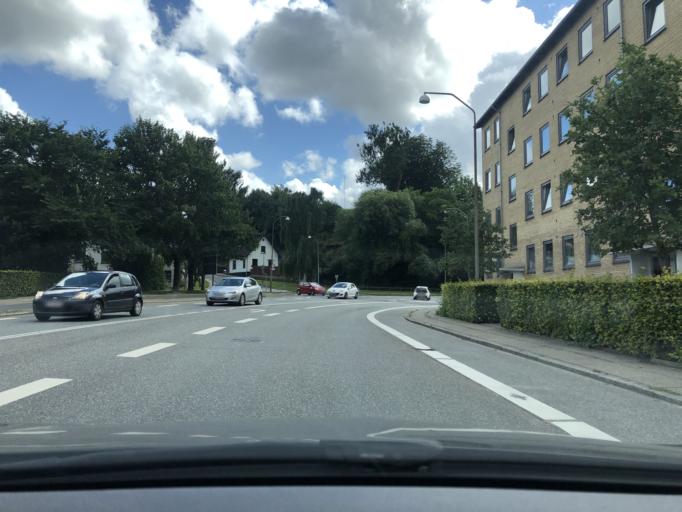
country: DK
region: South Denmark
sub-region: Vejle Kommune
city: Vejle
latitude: 55.7036
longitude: 9.5229
